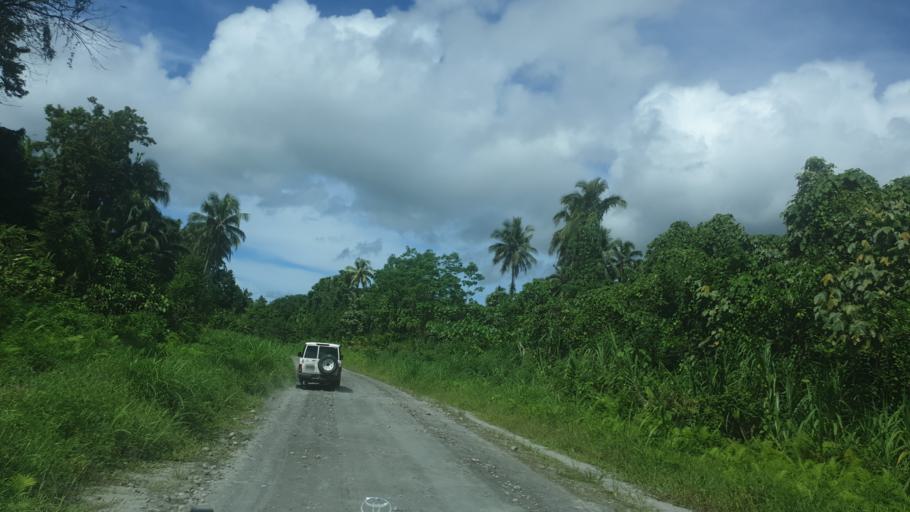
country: PG
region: Bougainville
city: Panguna
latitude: -6.5568
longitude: 155.3537
